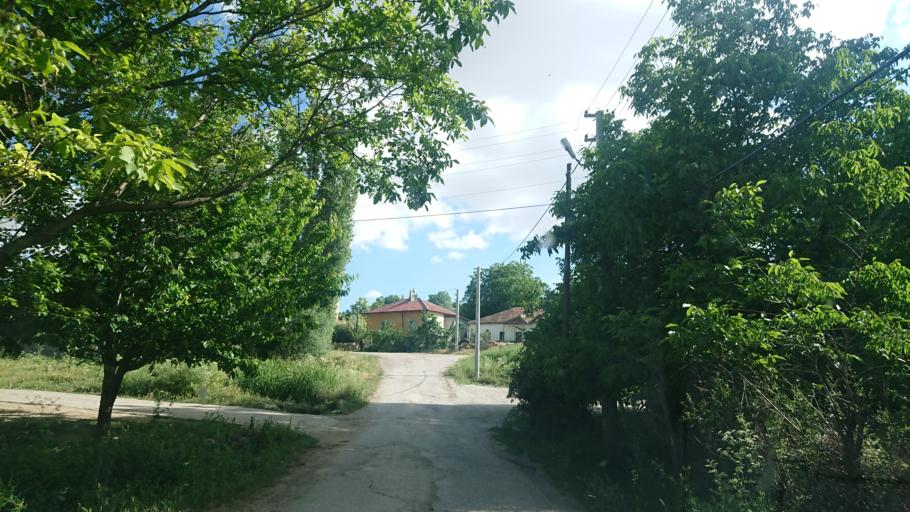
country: TR
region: Aksaray
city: Agacoren
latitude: 38.7525
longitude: 33.8877
